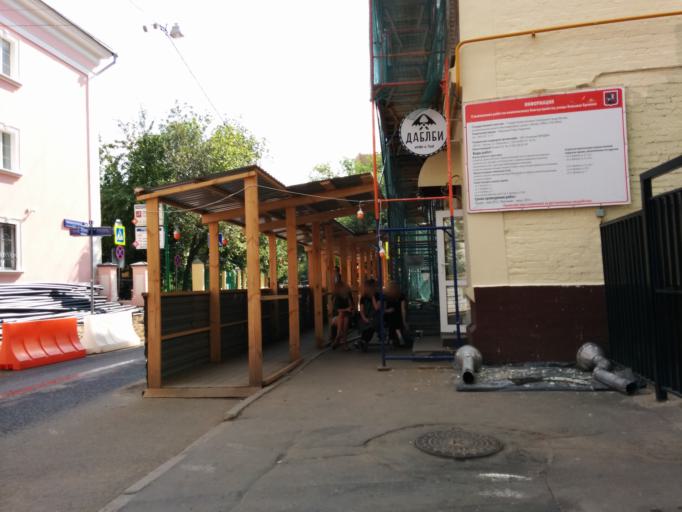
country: RU
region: Moscow
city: Moscow
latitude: 55.7626
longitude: 37.6002
